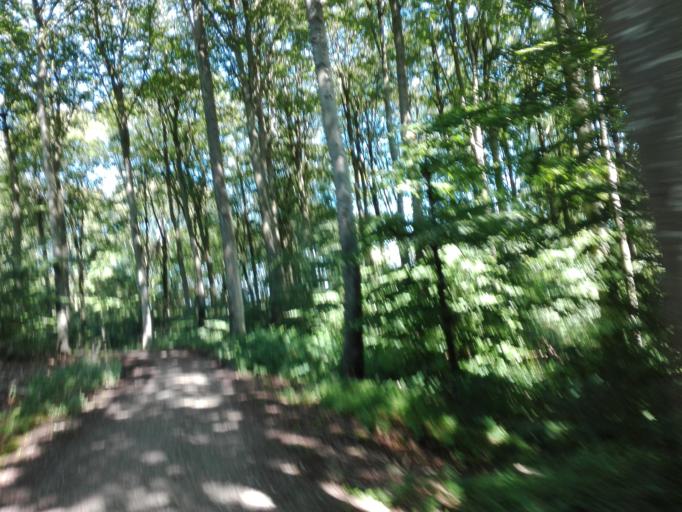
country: DK
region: Central Jutland
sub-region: Odder Kommune
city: Odder
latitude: 55.9563
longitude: 10.1510
